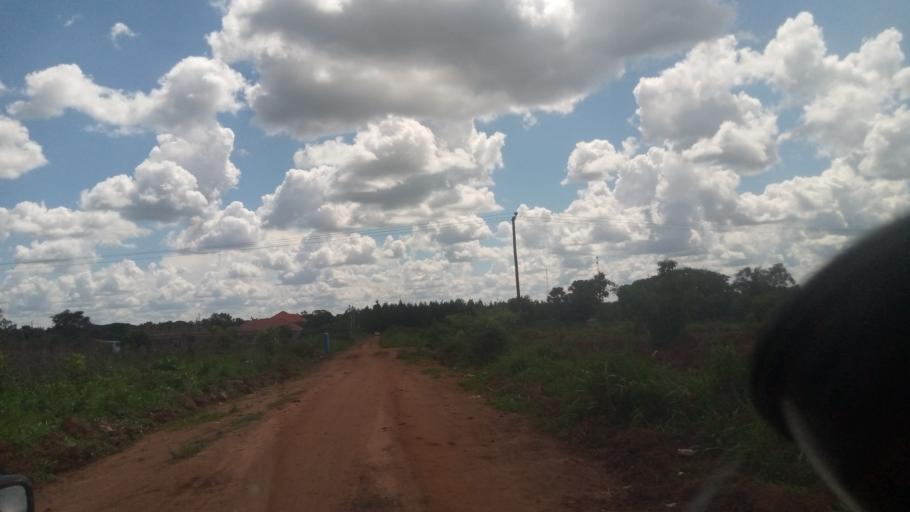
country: UG
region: Northern Region
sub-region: Lira District
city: Lira
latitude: 2.2320
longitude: 32.9044
